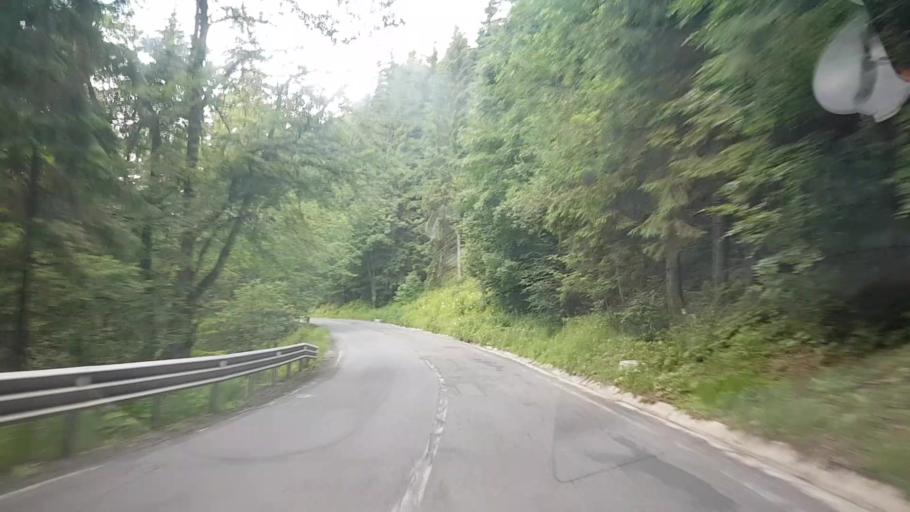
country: RO
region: Harghita
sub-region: Comuna Praid
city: Ocna de Sus
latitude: 46.6264
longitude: 25.2559
